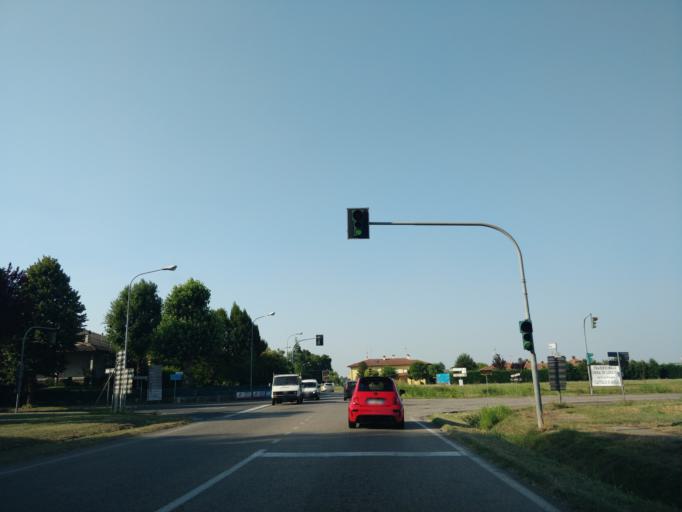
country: IT
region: Emilia-Romagna
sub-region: Provincia di Bologna
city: Castello d'Argile
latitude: 44.6790
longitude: 11.3009
